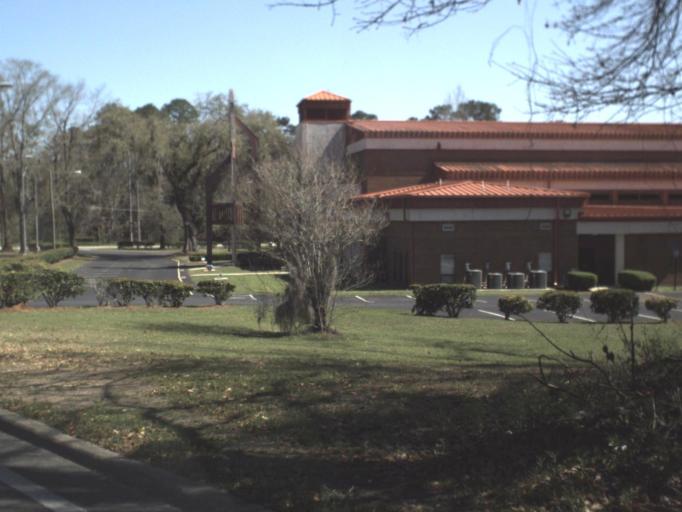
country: US
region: Florida
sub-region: Leon County
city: Tallahassee
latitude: 30.4125
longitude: -84.2912
